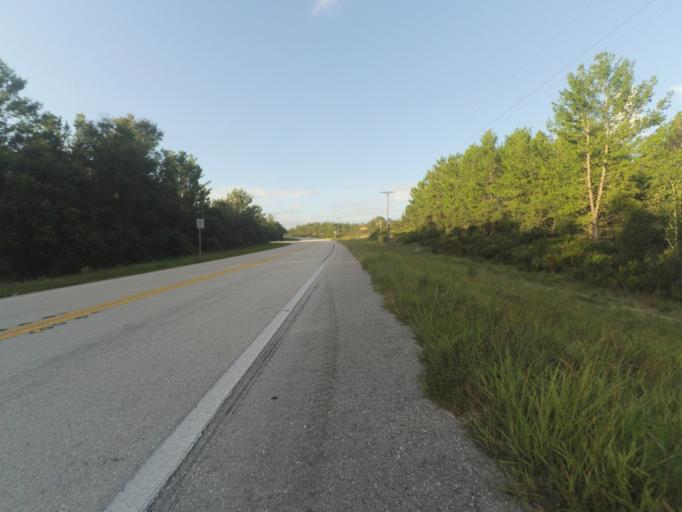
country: US
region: Florida
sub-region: Lake County
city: Astor
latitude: 29.2454
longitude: -81.6478
